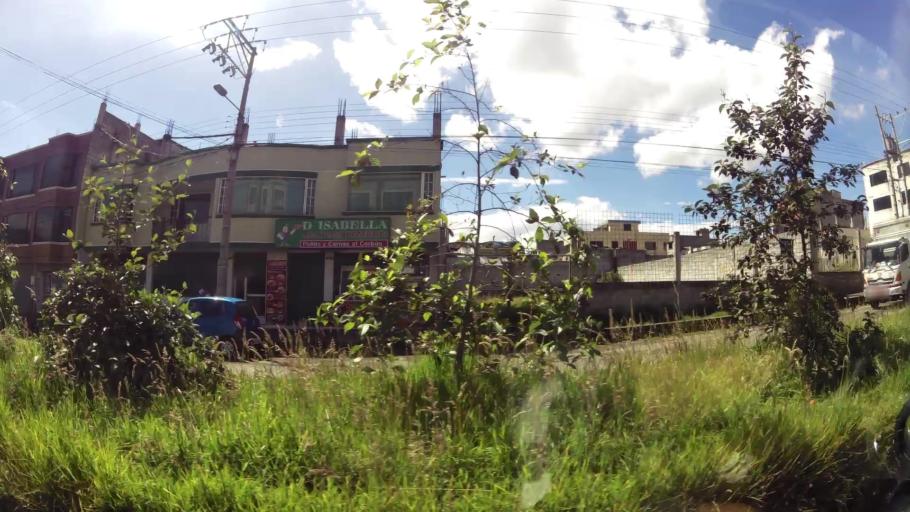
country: EC
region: Pichincha
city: Quito
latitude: -0.2994
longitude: -78.5473
